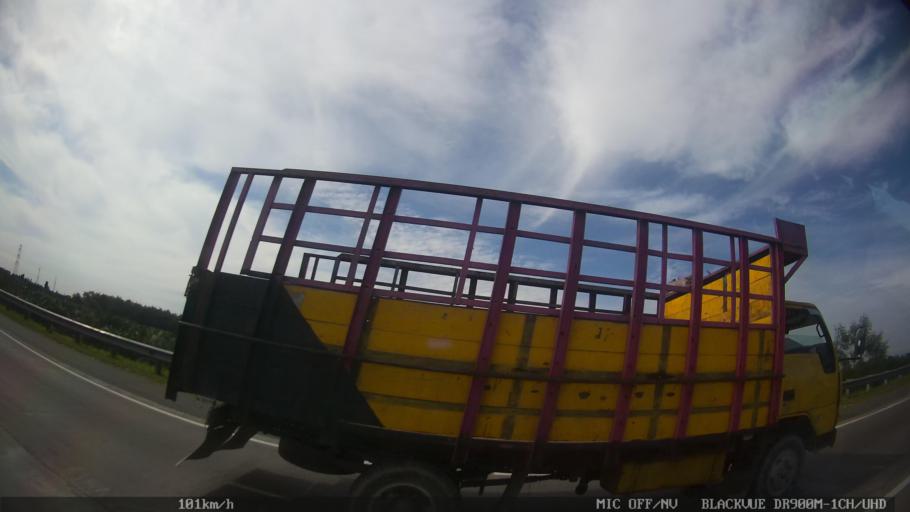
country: ID
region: North Sumatra
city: Sunggal
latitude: 3.6370
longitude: 98.5882
